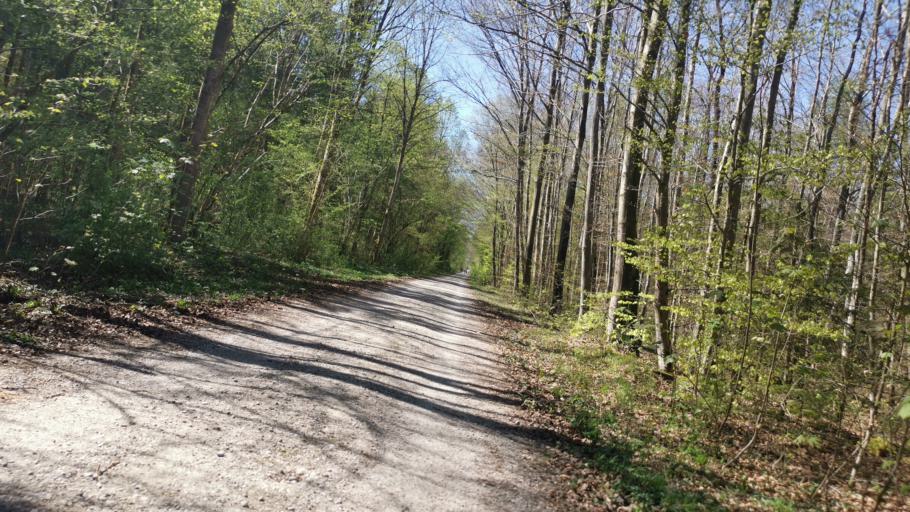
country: DE
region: Bavaria
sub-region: Upper Bavaria
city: Neuried
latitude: 48.0871
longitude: 11.4446
